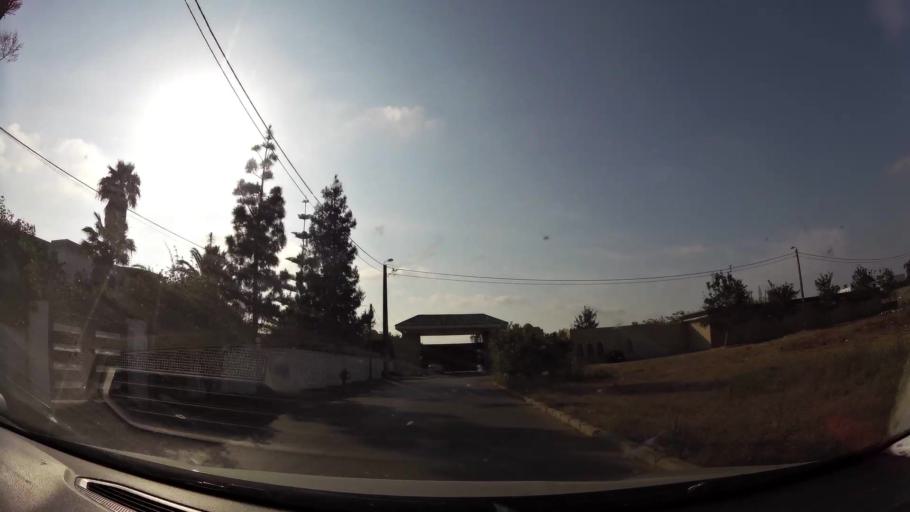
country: MA
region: Rabat-Sale-Zemmour-Zaer
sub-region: Rabat
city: Rabat
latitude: 33.9367
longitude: -6.8147
